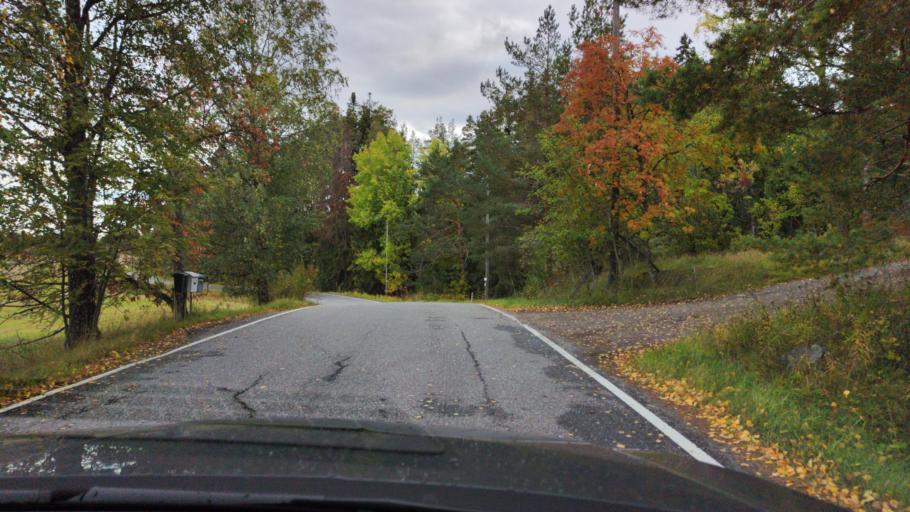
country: FI
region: Varsinais-Suomi
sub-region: Aboland-Turunmaa
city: Pargas
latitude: 60.3689
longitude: 22.2758
